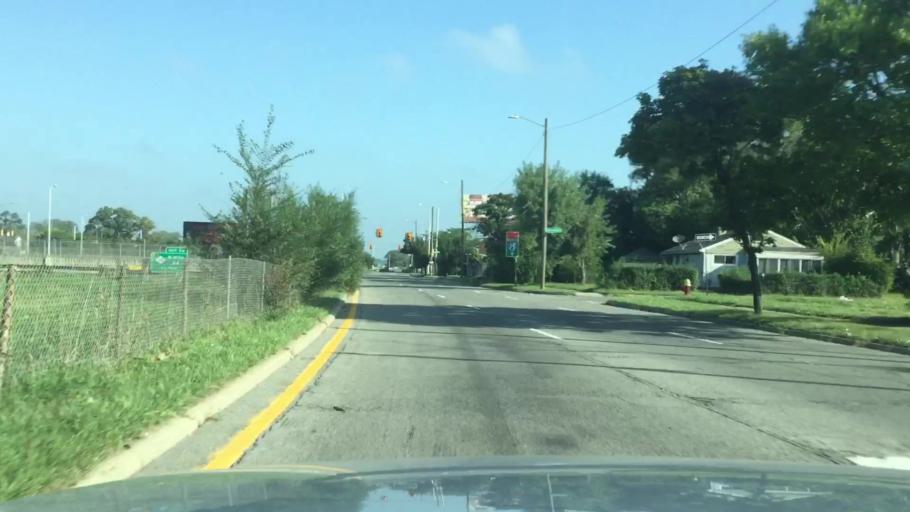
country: US
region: Michigan
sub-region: Wayne County
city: Highland Park
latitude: 42.4306
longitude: -83.0940
